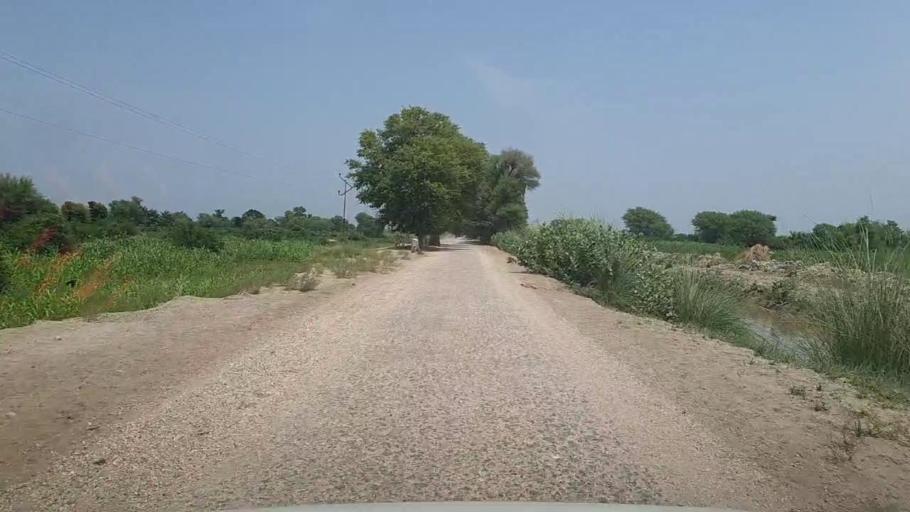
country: PK
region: Sindh
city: Karaundi
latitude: 26.9118
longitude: 68.3357
